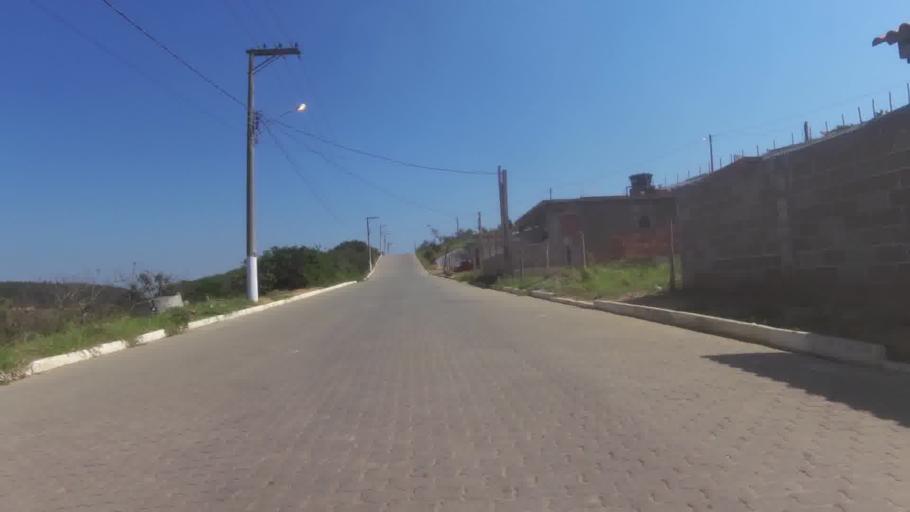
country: BR
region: Espirito Santo
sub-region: Itapemirim
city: Itapemirim
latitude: -21.0174
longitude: -40.8208
